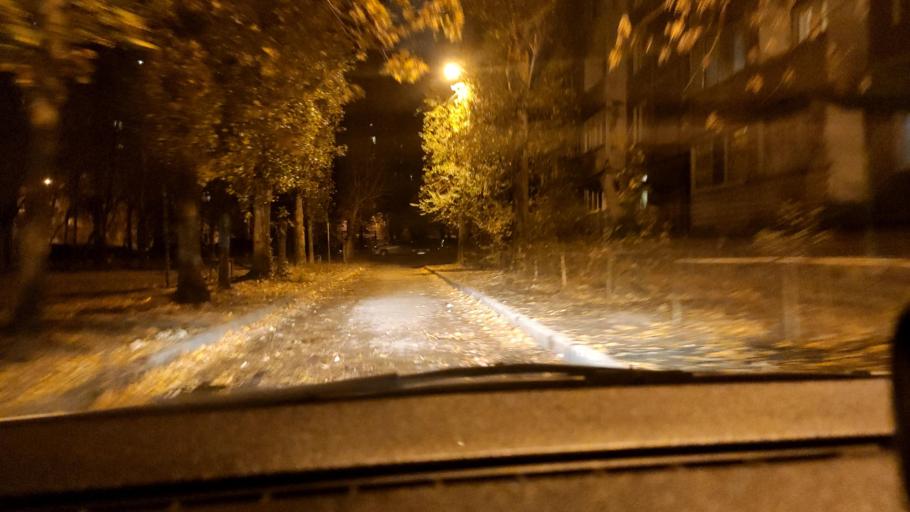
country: RU
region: Voronezj
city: Pridonskoy
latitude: 51.6591
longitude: 39.1134
